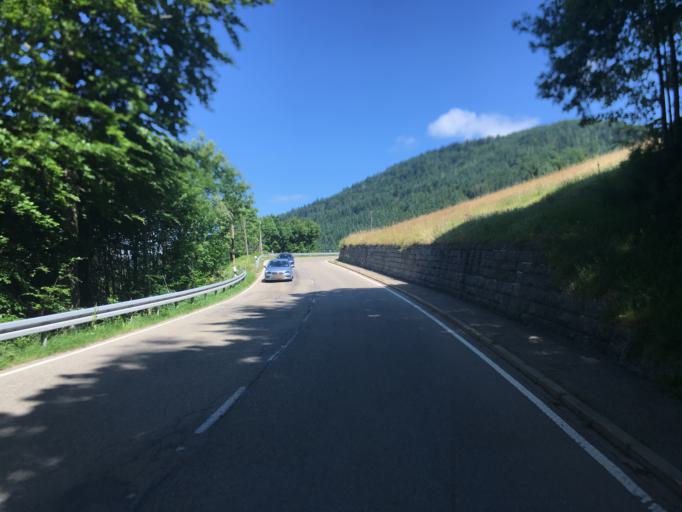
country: DE
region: Baden-Wuerttemberg
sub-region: Freiburg Region
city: Seebach
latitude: 48.5763
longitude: 8.2039
